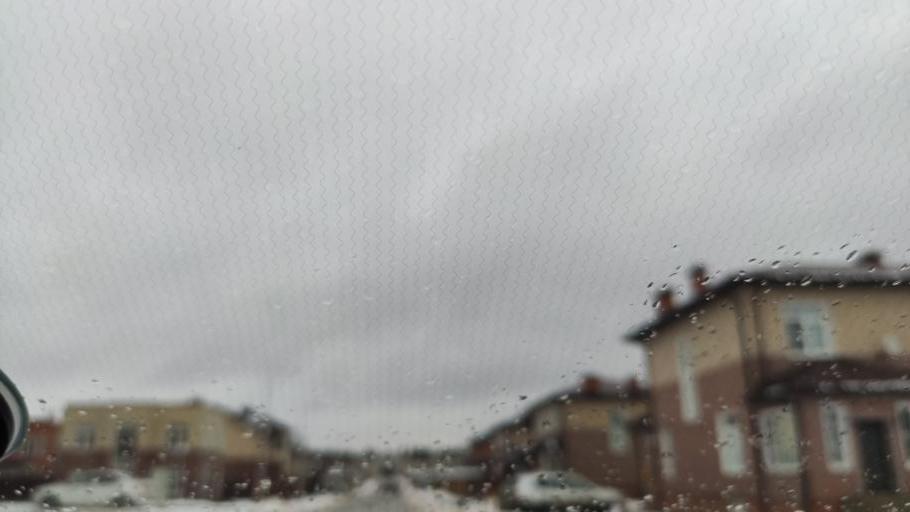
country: RU
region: Moskovskaya
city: Vatutinki
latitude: 55.4270
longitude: 37.3817
